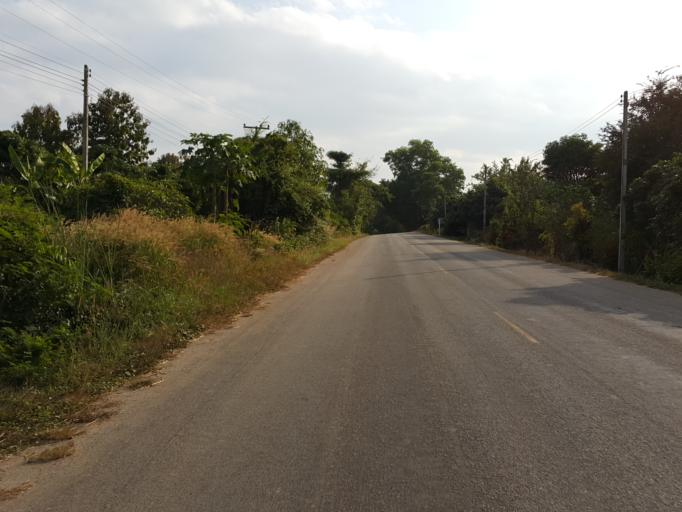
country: TH
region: Lamphun
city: Thung Hua Chang
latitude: 18.1221
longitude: 99.0146
